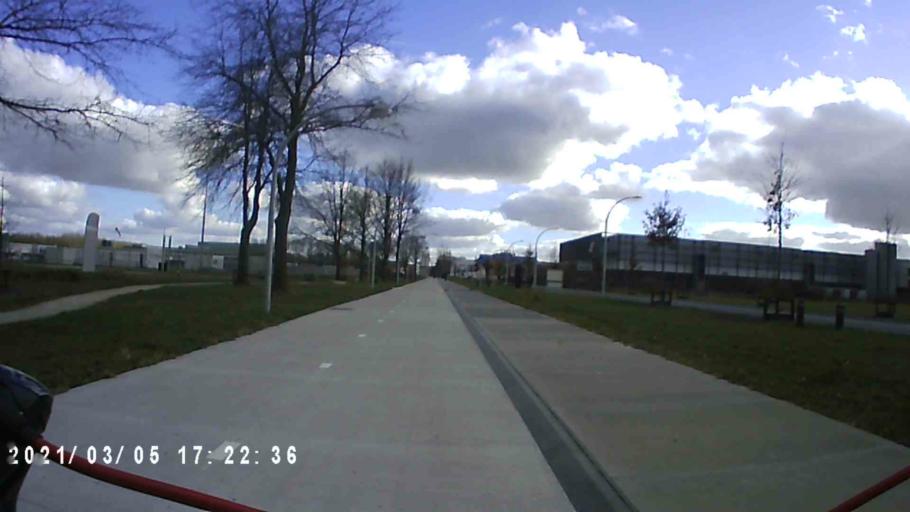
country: NL
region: Groningen
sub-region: Gemeente Groningen
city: Korrewegwijk
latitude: 53.2476
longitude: 6.5285
